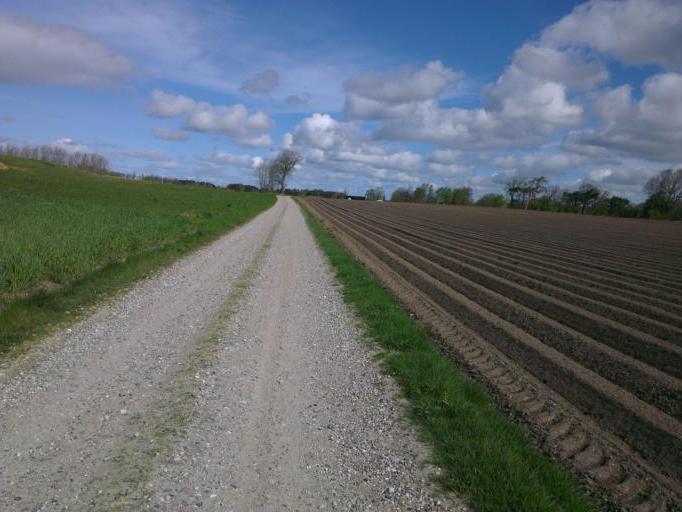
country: DK
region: Capital Region
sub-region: Frederikssund Kommune
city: Jaegerspris
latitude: 55.8126
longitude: 12.0081
